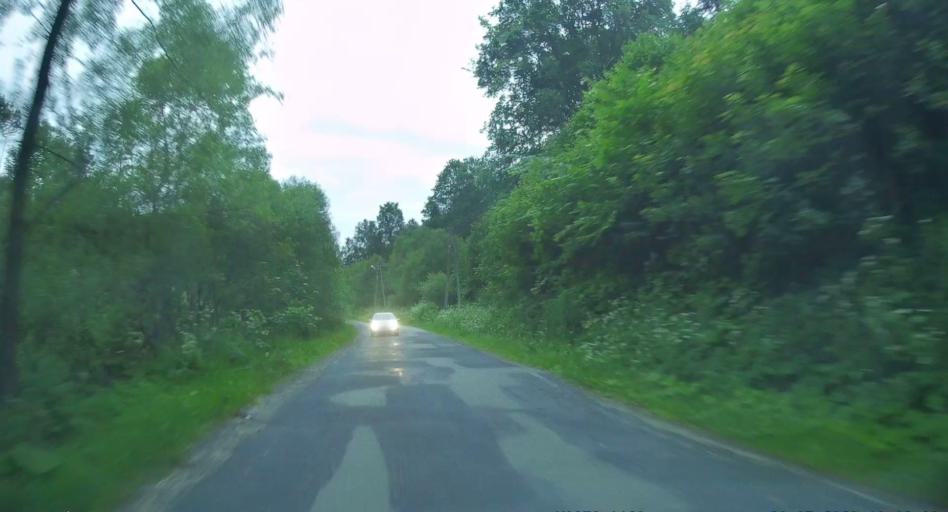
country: PL
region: Lesser Poland Voivodeship
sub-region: Powiat nowosadecki
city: Muszyna
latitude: 49.3684
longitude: 20.9247
